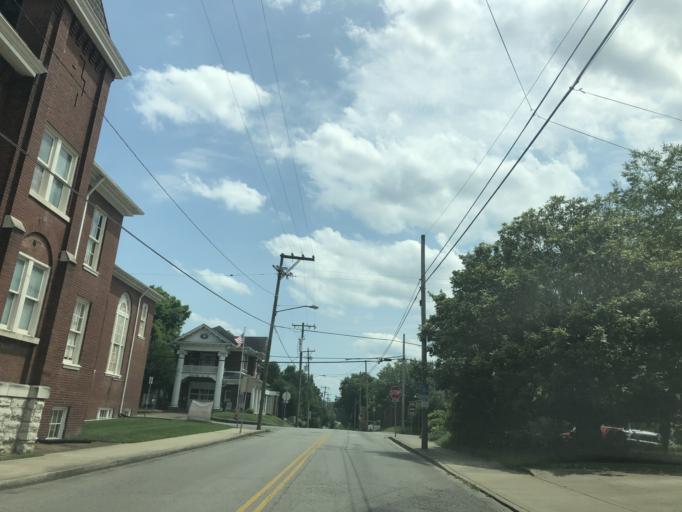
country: US
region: Tennessee
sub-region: Davidson County
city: Nashville
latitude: 36.1760
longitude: -86.7421
